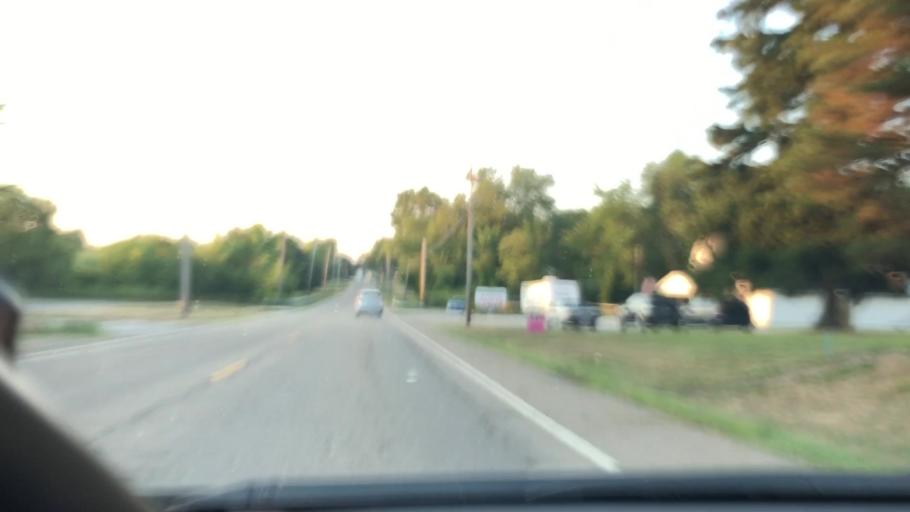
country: US
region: Ohio
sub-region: Summit County
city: Greensburg
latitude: 40.9341
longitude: -81.4648
